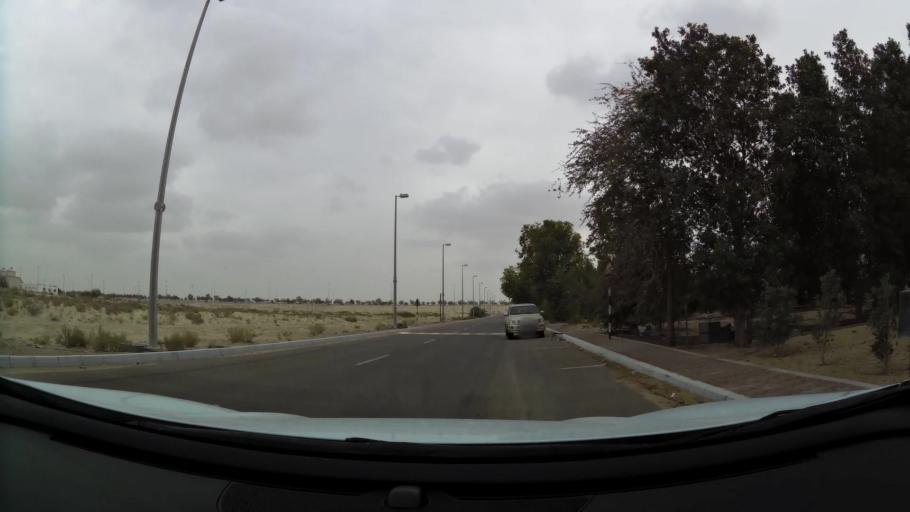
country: AE
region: Abu Dhabi
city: Abu Dhabi
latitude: 24.3882
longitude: 54.6561
